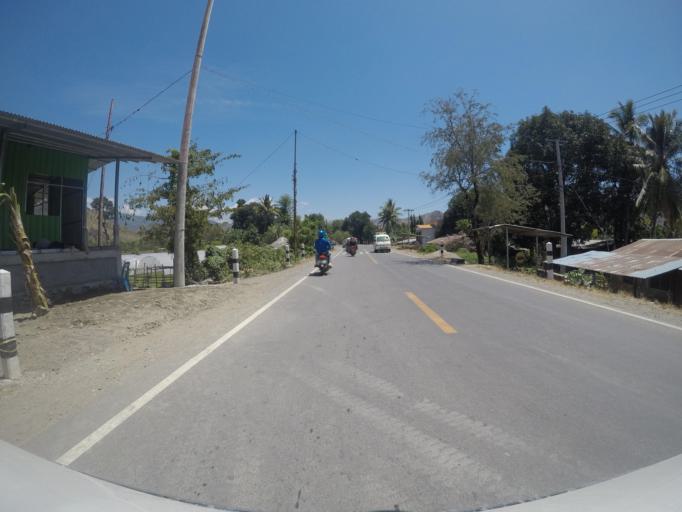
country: ID
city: Metinaro
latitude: -8.5419
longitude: 125.6776
